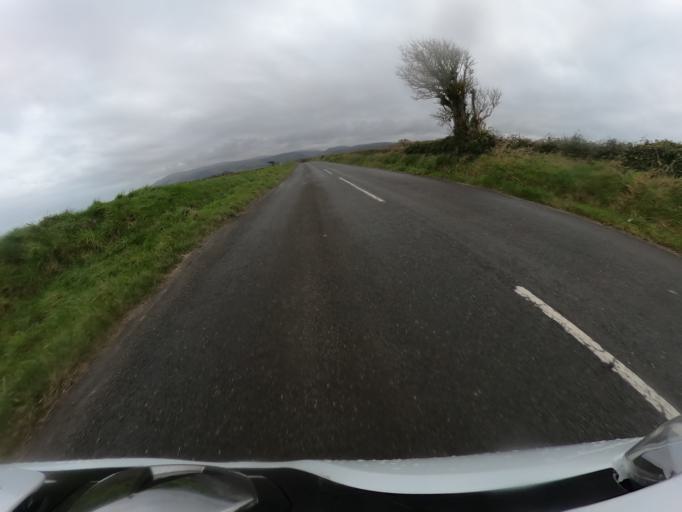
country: IM
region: Ramsey
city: Ramsey
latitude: 54.3535
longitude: -4.5072
